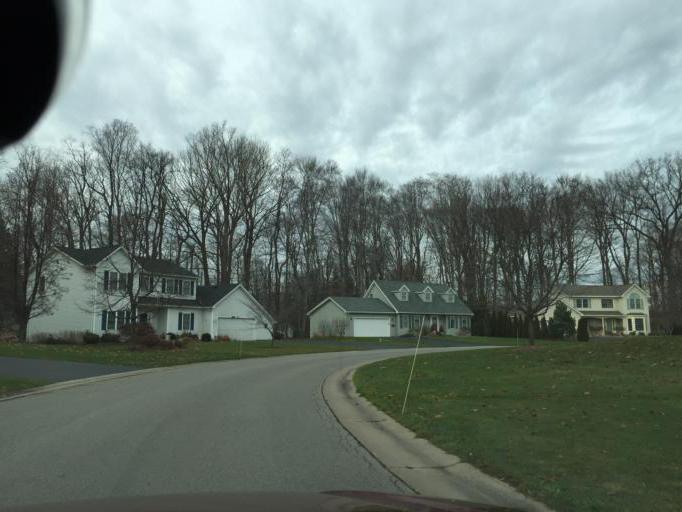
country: US
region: New York
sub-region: Monroe County
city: North Gates
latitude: 43.1119
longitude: -77.7238
